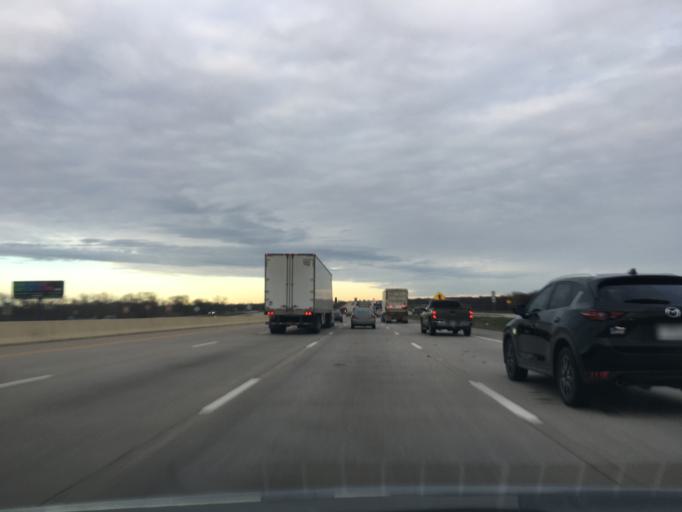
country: US
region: Texas
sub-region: Collin County
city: McKinney
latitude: 33.2465
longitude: -96.6229
